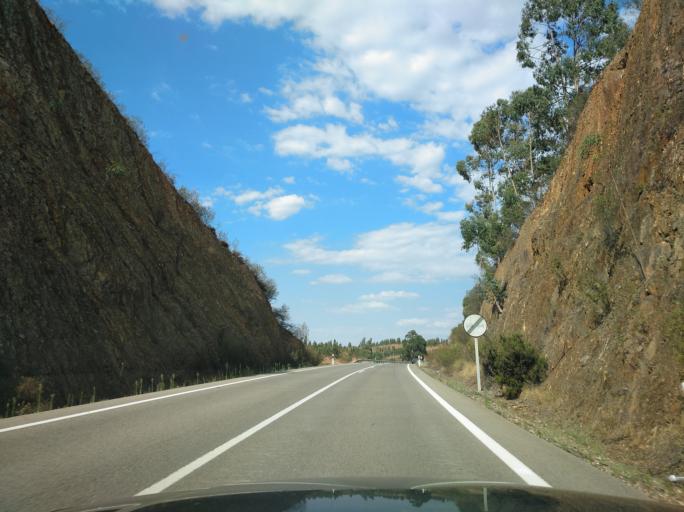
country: ES
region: Andalusia
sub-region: Provincia de Huelva
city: Santa Barbara de Casa
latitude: 37.8805
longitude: -7.2110
